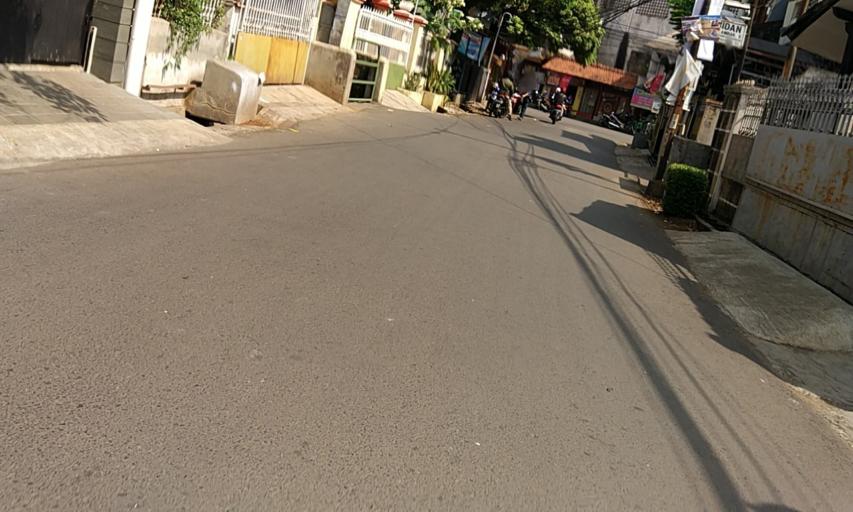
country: ID
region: West Java
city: Bandung
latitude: -6.9059
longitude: 107.6863
